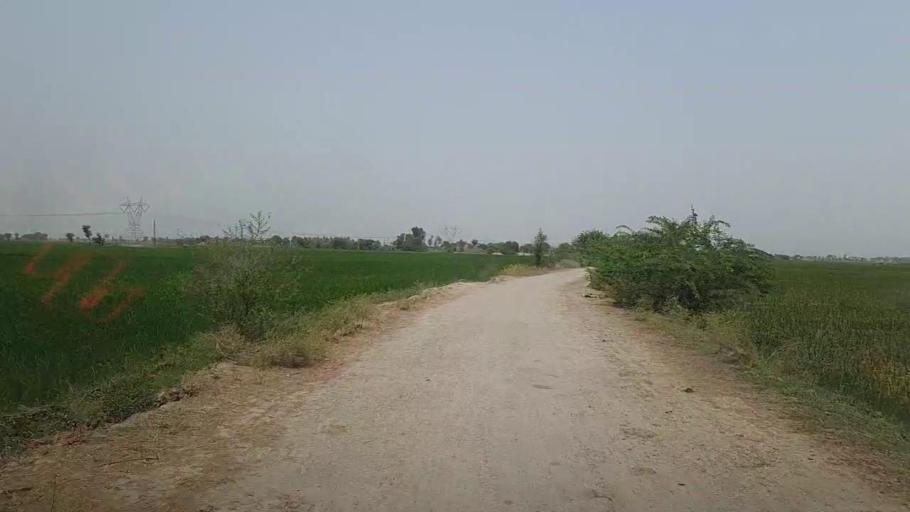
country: PK
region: Sindh
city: Sita Road
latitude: 27.0629
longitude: 67.8489
